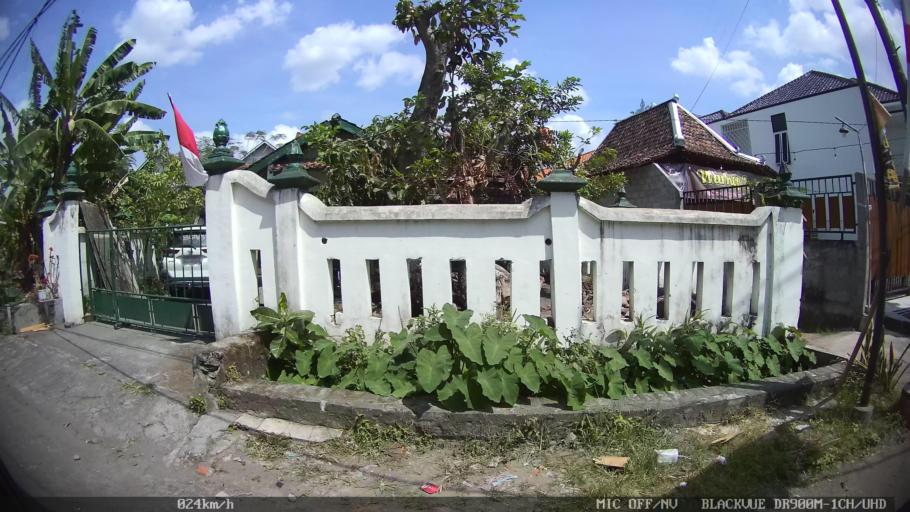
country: ID
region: Daerah Istimewa Yogyakarta
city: Sewon
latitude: -7.8326
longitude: 110.3862
